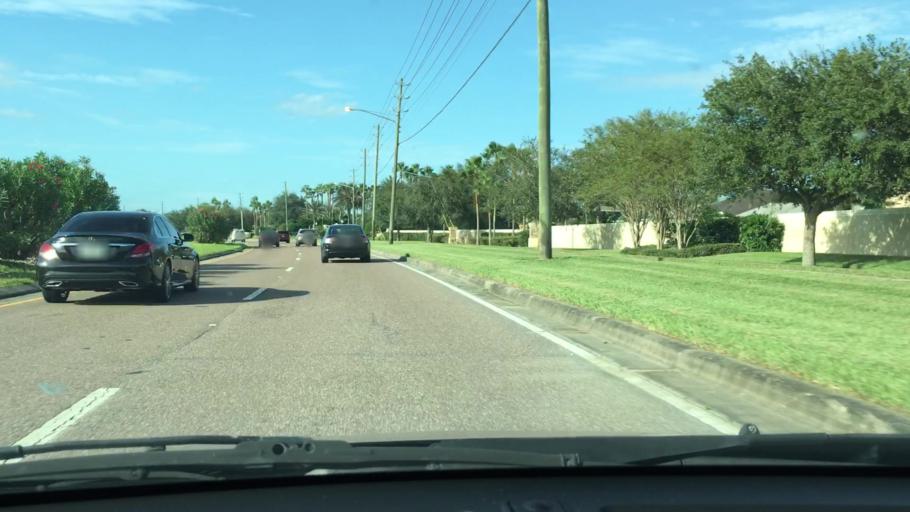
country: US
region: Florida
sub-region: Pasco County
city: Land O' Lakes
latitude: 28.2058
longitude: -82.4334
